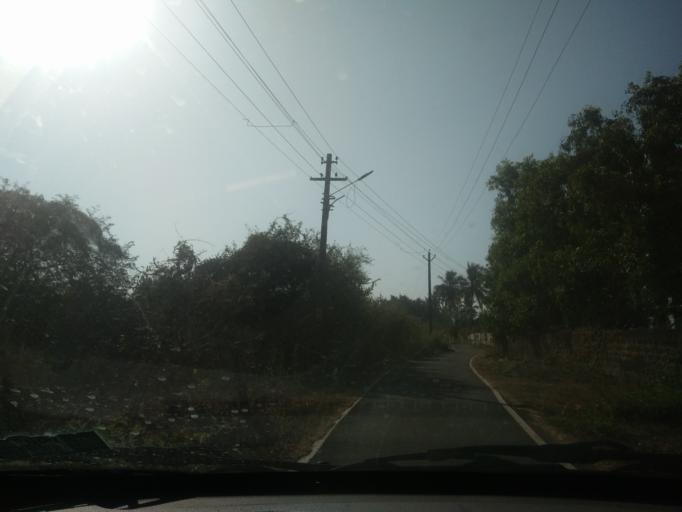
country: IN
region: Goa
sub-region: South Goa
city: Sancoale
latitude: 15.3512
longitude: 73.8883
